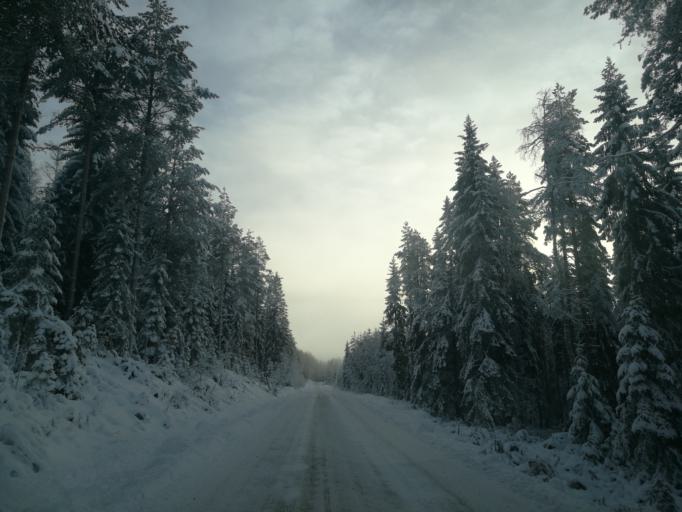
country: SE
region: Vaermland
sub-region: Torsby Kommun
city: Torsby
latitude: 60.6486
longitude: 12.7249
